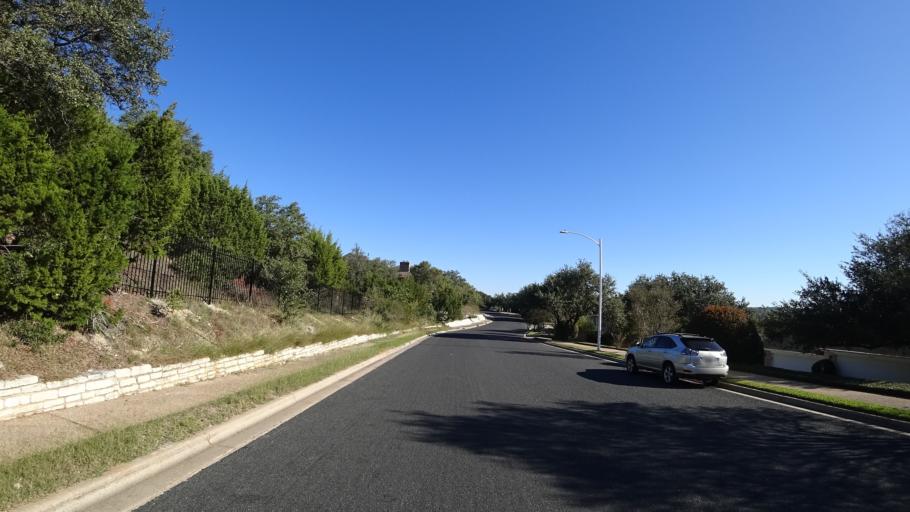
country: US
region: Texas
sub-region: Travis County
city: West Lake Hills
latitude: 30.3357
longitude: -97.8012
